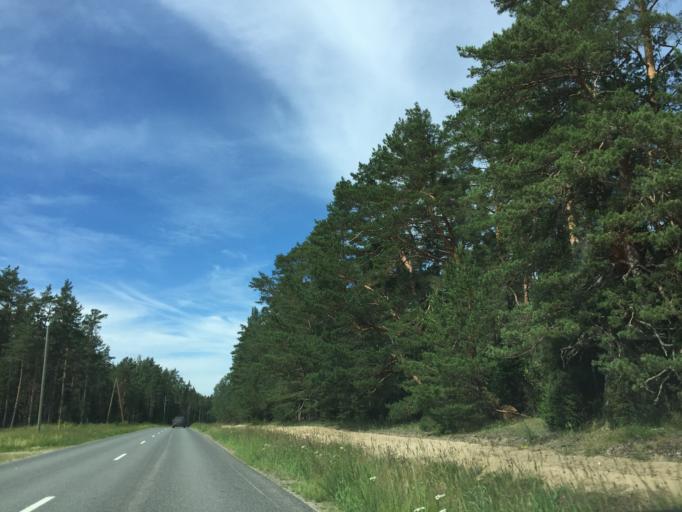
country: LV
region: Dundaga
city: Dundaga
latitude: 57.6315
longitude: 22.5704
